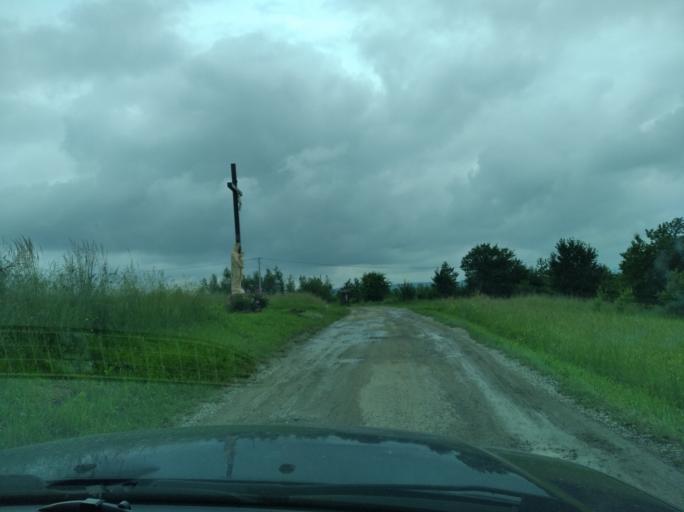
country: PL
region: Subcarpathian Voivodeship
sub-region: Powiat jaroslawski
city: Pruchnik
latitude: 49.8870
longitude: 22.5171
